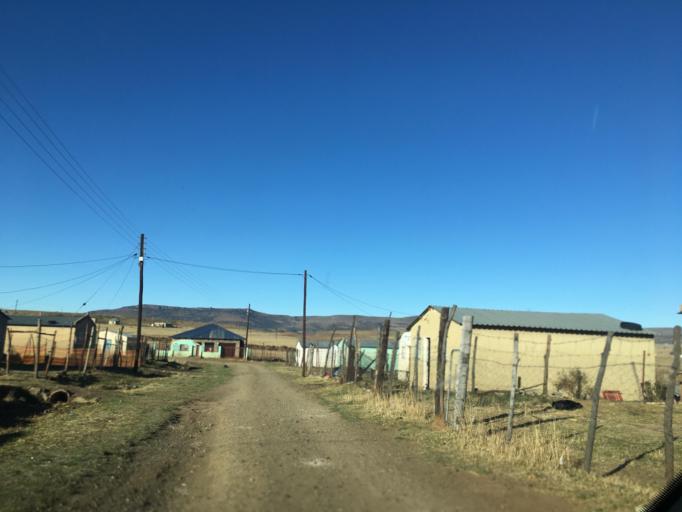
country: ZA
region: Eastern Cape
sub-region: Chris Hani District Municipality
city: Cala
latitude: -31.5409
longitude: 27.6777
